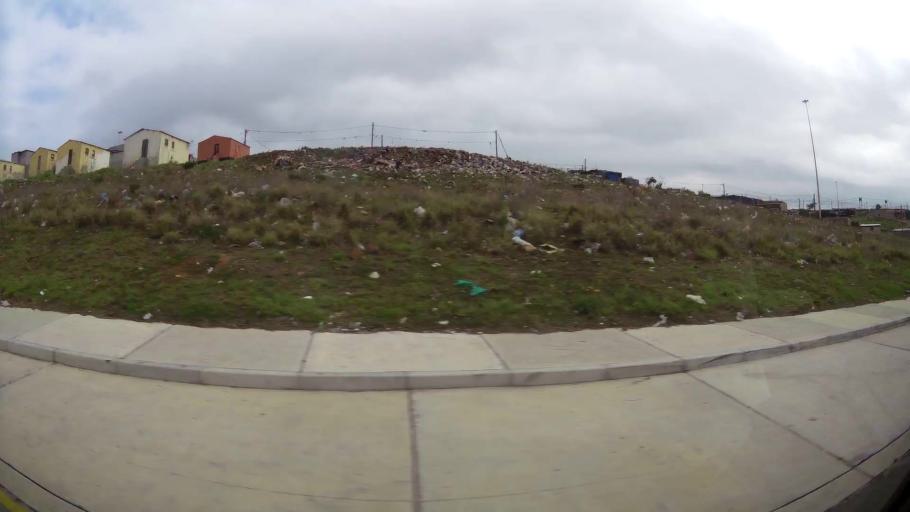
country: ZA
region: Eastern Cape
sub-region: Nelson Mandela Bay Metropolitan Municipality
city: Port Elizabeth
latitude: -33.9124
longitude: 25.5383
